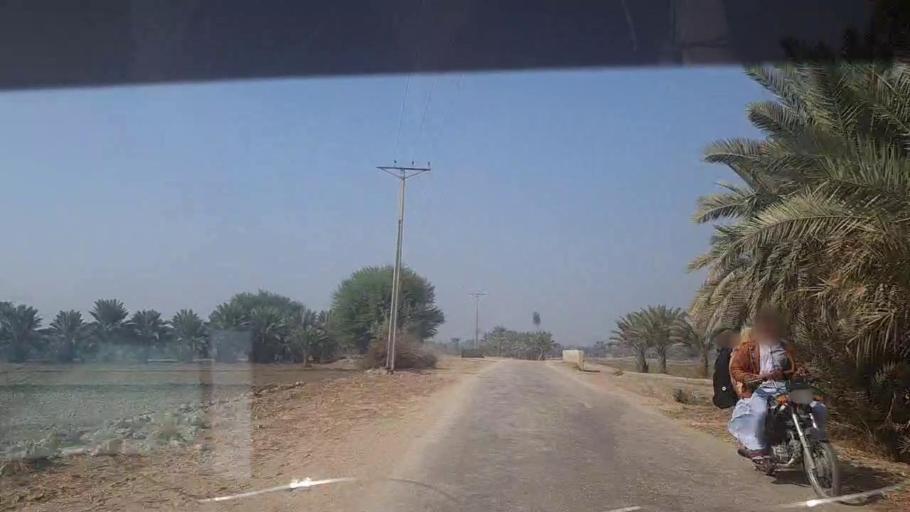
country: PK
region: Sindh
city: Kot Diji
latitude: 27.3732
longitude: 68.6978
